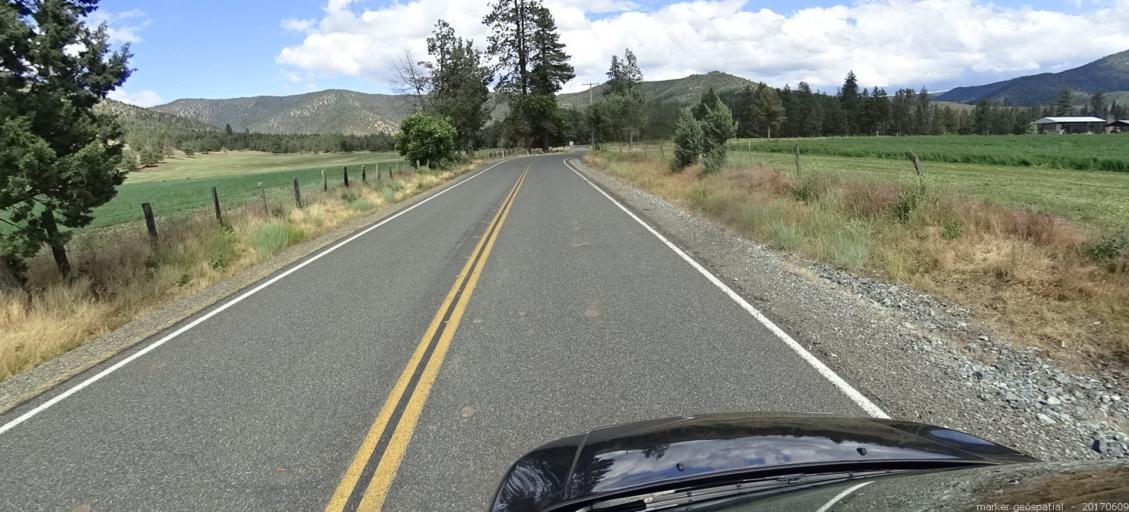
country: US
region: California
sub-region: Siskiyou County
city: Yreka
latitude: 41.5013
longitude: -122.8321
